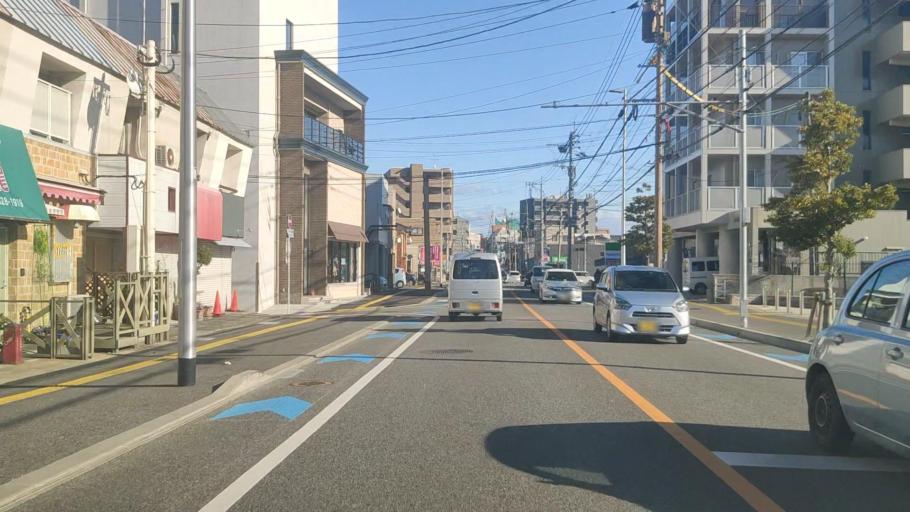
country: JP
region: Fukuoka
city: Fukuoka-shi
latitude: 33.5534
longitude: 130.3561
